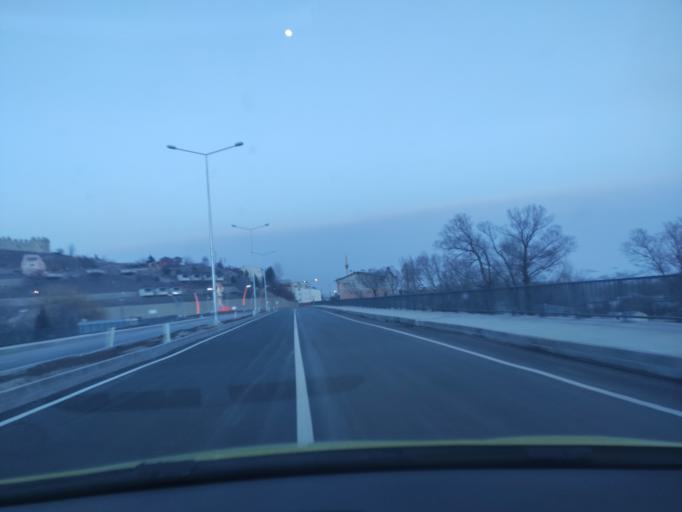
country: TR
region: Bayburt
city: Aydintepe
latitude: 40.3888
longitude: 40.1457
